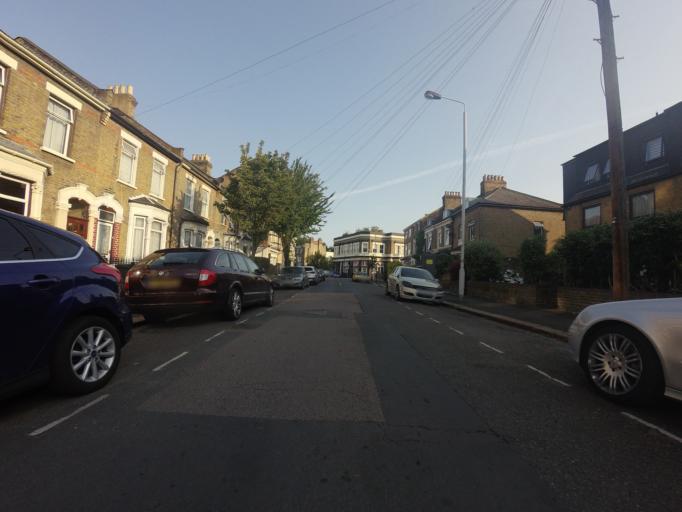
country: GB
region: England
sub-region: Greater London
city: Walthamstow
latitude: 51.5560
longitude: 0.0004
